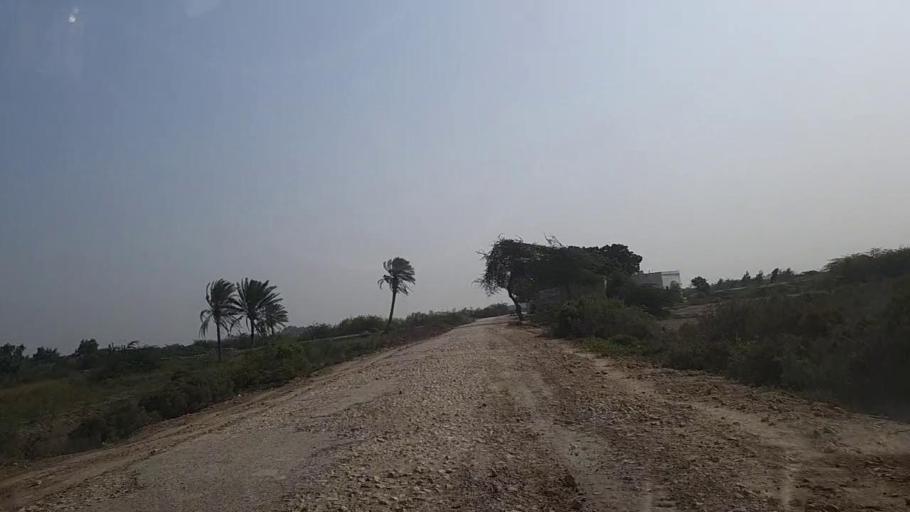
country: PK
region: Sindh
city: Keti Bandar
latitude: 24.2450
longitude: 67.6355
